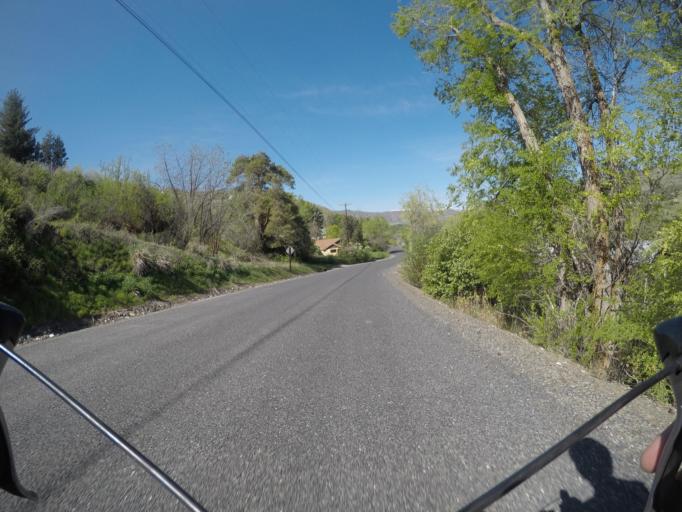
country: US
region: Washington
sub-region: Chelan County
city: West Wenatchee
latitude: 47.4773
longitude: -120.3873
